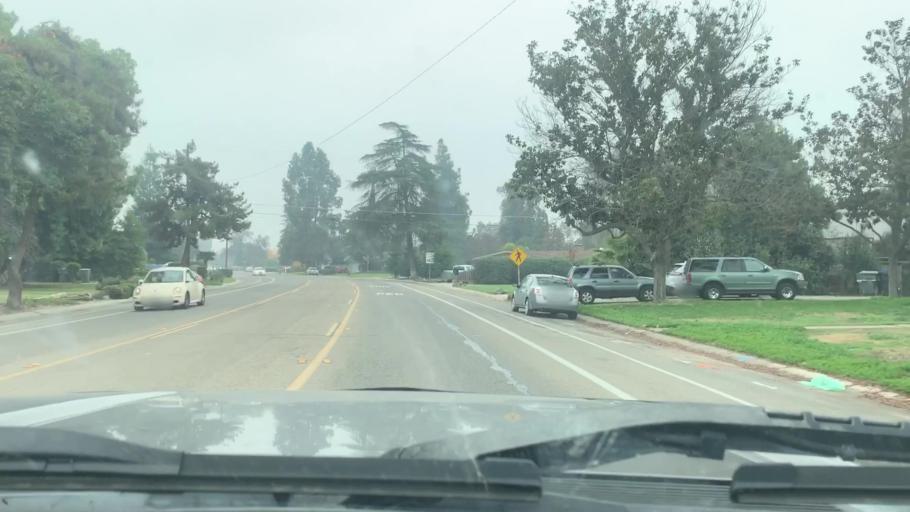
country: US
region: California
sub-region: Tulare County
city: Visalia
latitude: 36.3178
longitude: -119.3268
